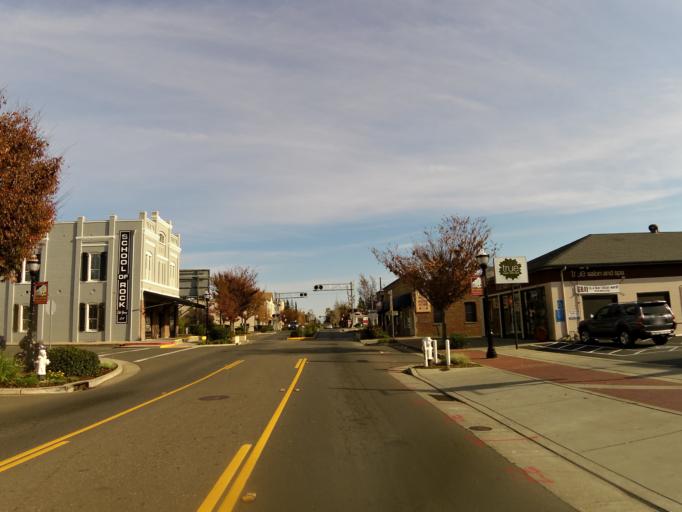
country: US
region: California
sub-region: Sacramento County
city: Elk Grove
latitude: 38.4090
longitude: -121.3655
